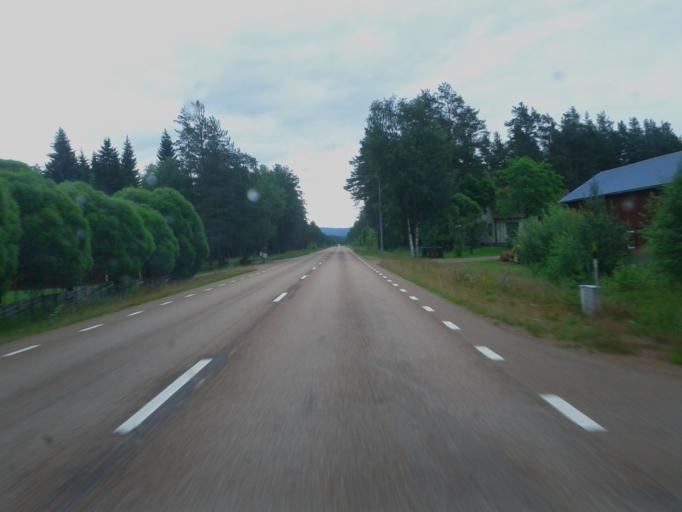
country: SE
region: Dalarna
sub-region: Alvdalens Kommun
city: AElvdalen
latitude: 61.2763
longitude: 13.9663
